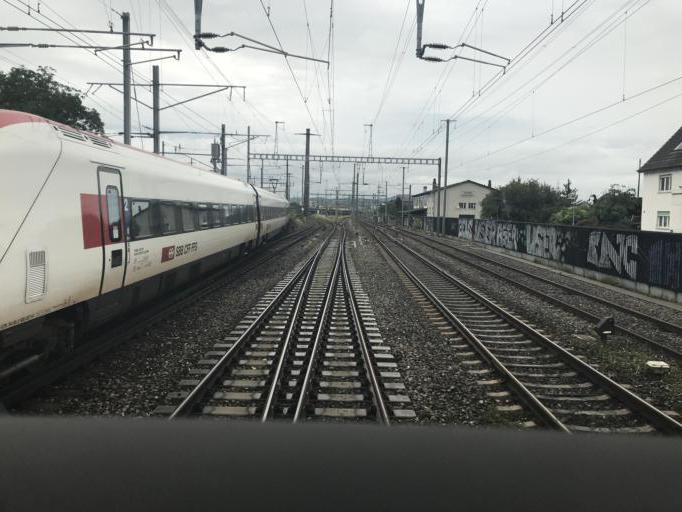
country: CH
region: Zurich
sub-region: Bezirk Zuerich
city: Zuerich (Kreis 11) / Seebach
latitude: 47.4163
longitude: 8.5497
